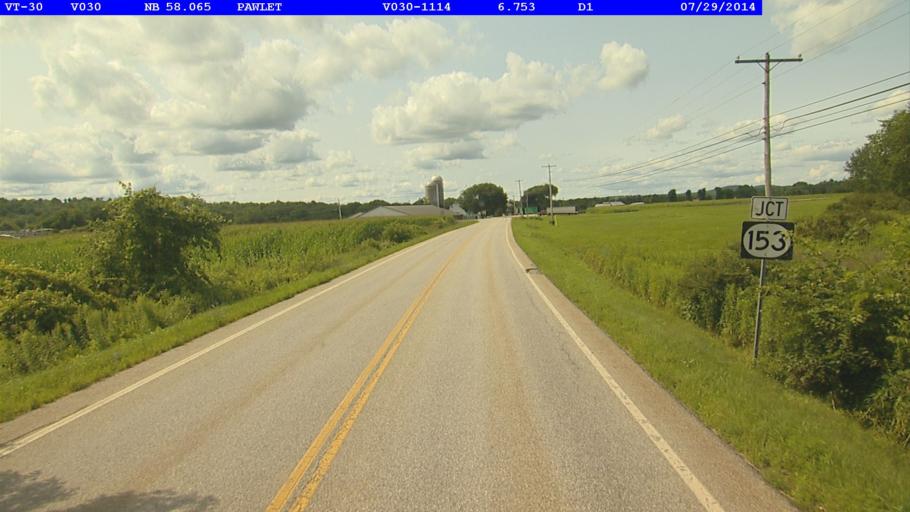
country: US
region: New York
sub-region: Washington County
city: Granville
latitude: 43.3877
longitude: -73.2185
